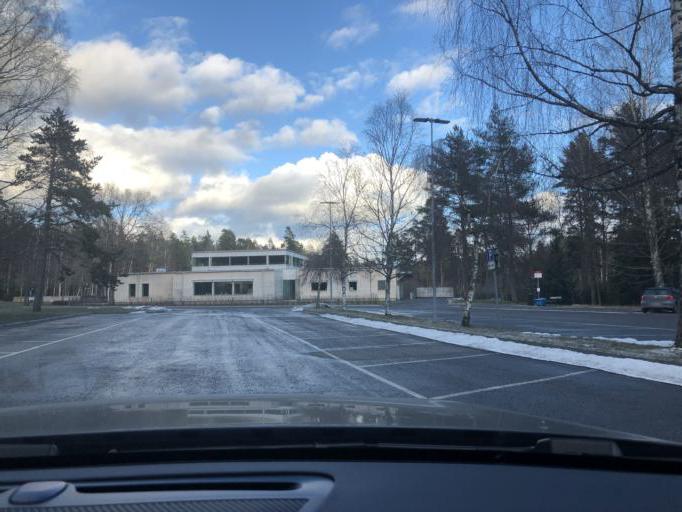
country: SE
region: Stockholm
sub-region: Botkyrka Kommun
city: Fittja
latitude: 59.2361
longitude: 17.8910
